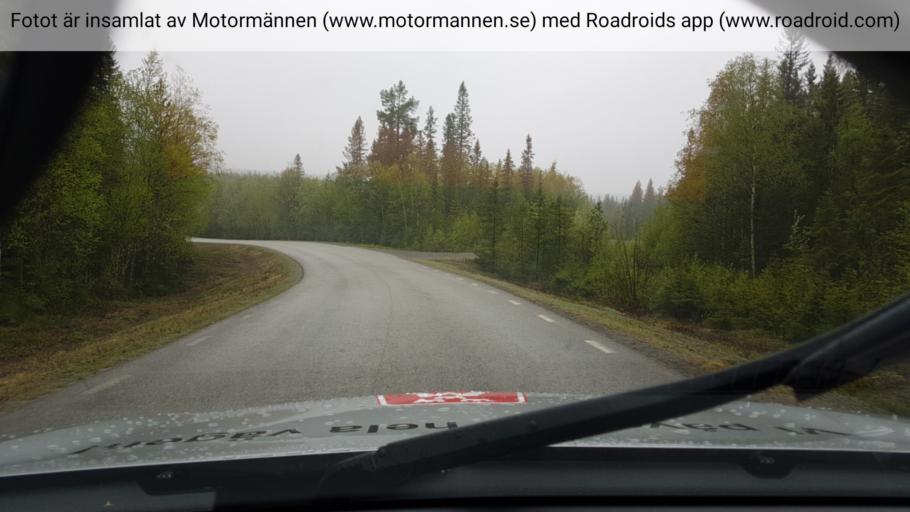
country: SE
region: Jaemtland
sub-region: Bergs Kommun
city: Hoverberg
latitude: 63.0420
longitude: 14.0131
